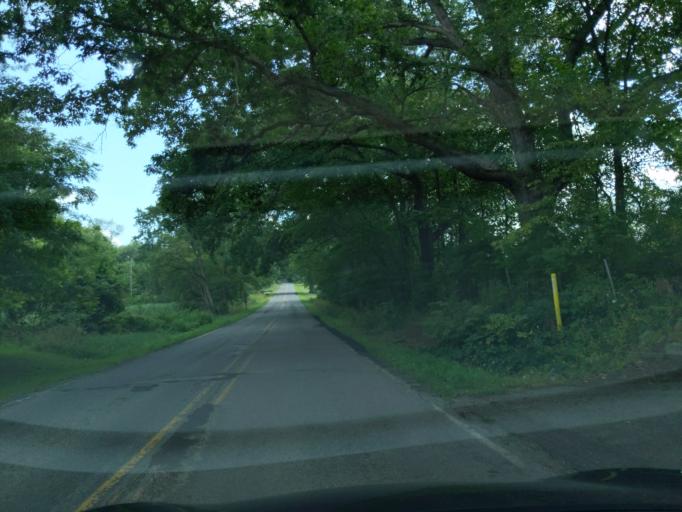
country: US
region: Michigan
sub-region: Jackson County
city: Spring Arbor
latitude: 42.3141
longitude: -84.5198
